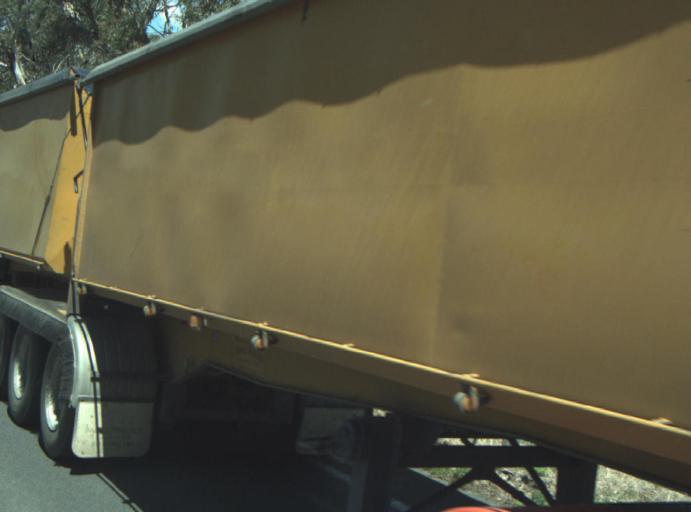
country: AU
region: Victoria
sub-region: Greater Geelong
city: Lara
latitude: -37.8882
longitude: 144.2569
